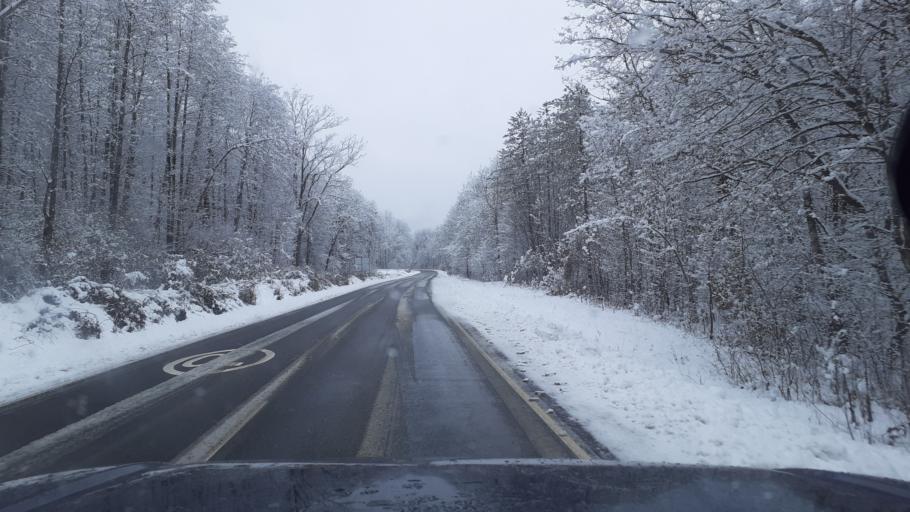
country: RU
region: Adygeya
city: Kamennomostskiy
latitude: 44.1898
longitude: 40.1670
